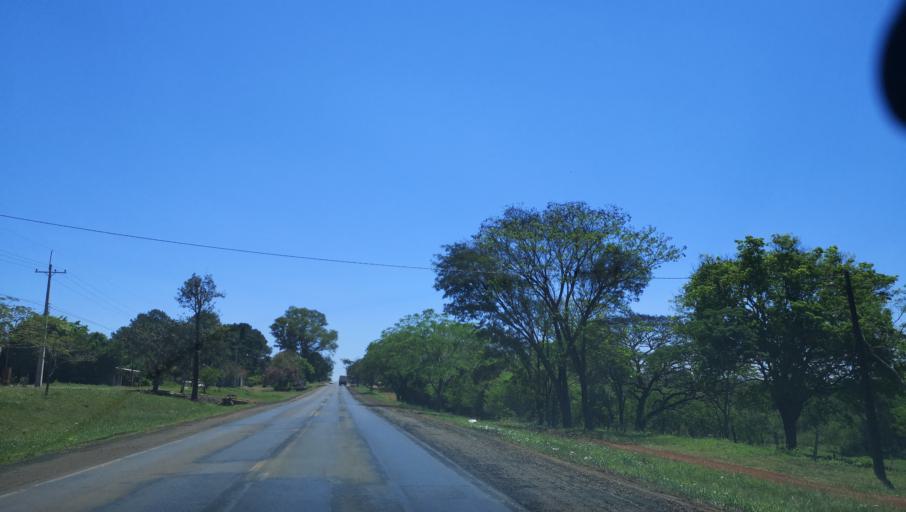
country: PY
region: Itapua
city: San Juan del Parana
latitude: -27.2493
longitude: -55.9911
